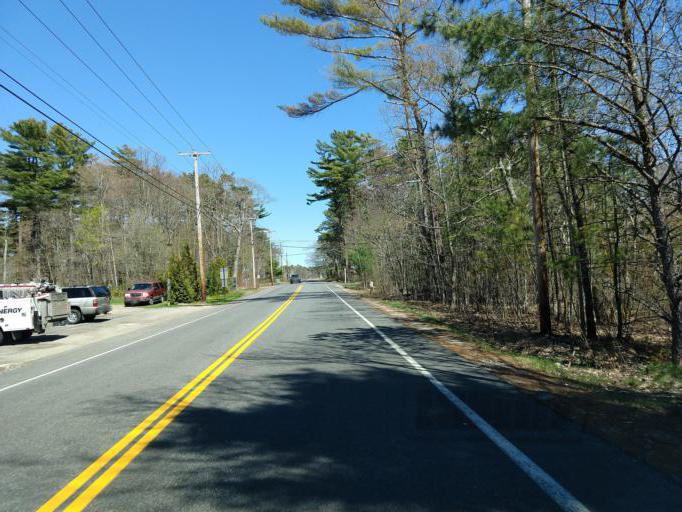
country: US
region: Maine
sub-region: York County
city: Kennebunk
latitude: 43.3508
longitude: -70.5237
